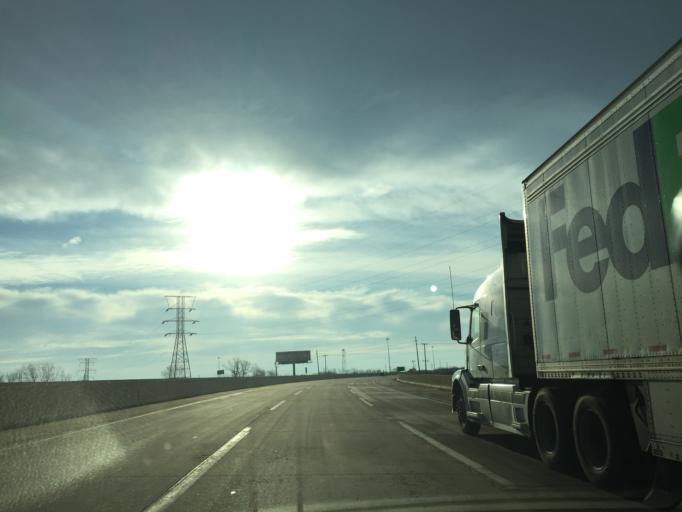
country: US
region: Indiana
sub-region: Lake County
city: Gary
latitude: 41.6003
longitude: -87.3084
